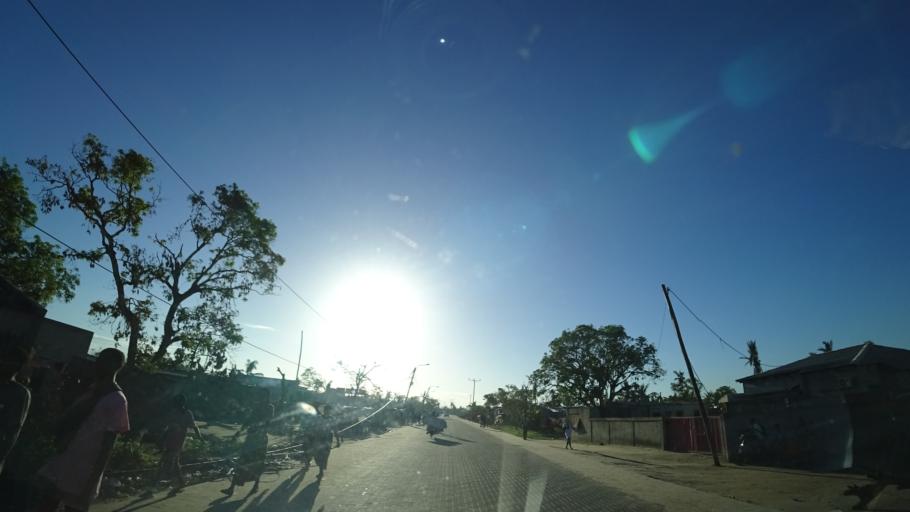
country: MZ
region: Sofala
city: Beira
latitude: -19.7448
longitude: 34.8454
